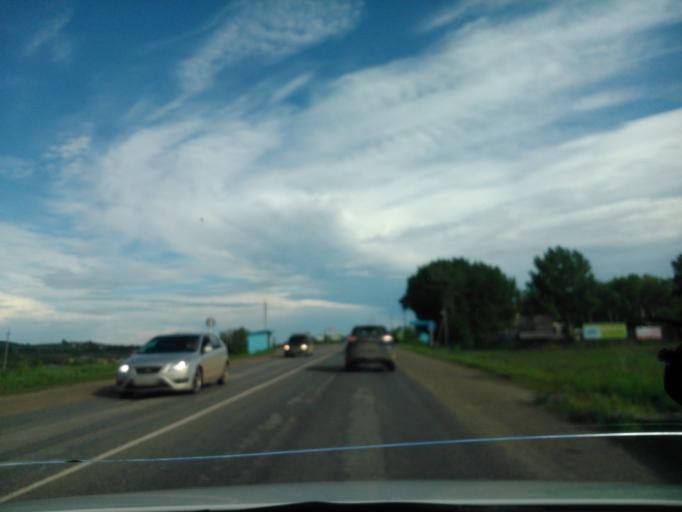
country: RU
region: Perm
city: Lobanovo
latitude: 57.8676
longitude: 56.2885
